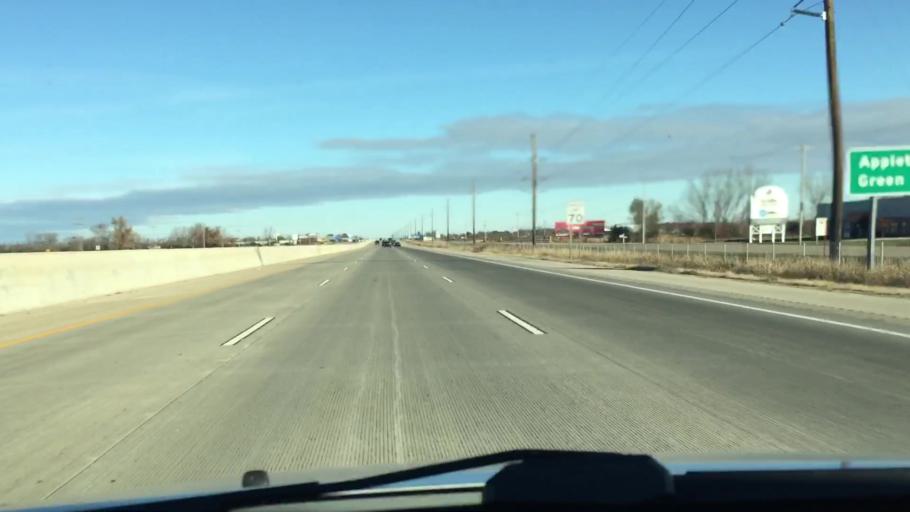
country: US
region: Wisconsin
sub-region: Winnebago County
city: Oshkosh
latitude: 43.9597
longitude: -88.5829
